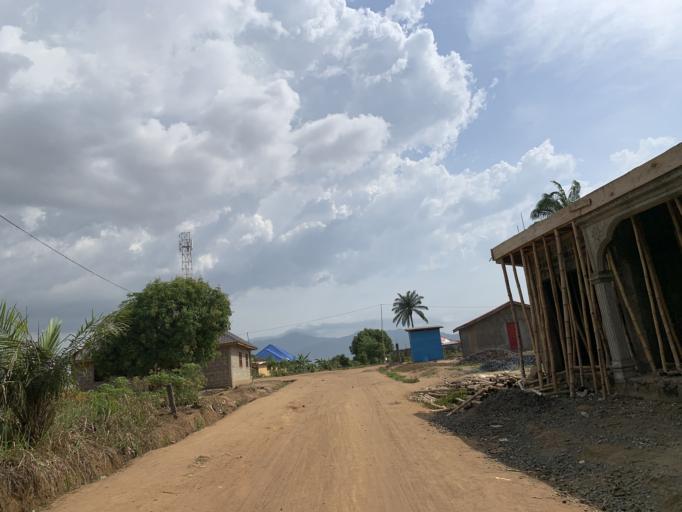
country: SL
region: Western Area
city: Waterloo
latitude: 8.3471
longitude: -13.0396
